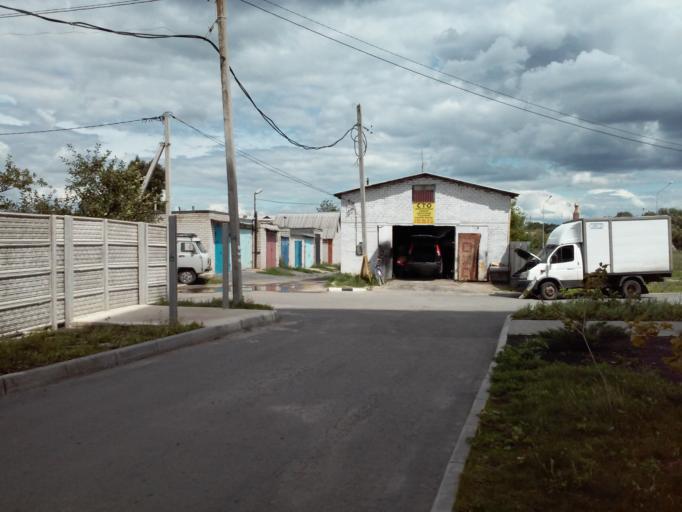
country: RU
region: Belgorod
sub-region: Belgorodskiy Rayon
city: Belgorod
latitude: 50.5364
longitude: 36.5792
